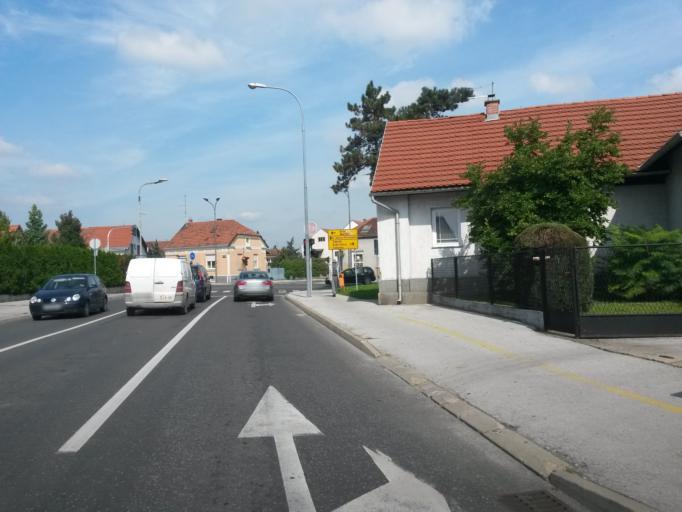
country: HR
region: Varazdinska
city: Varazdin
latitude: 46.3142
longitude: 16.3271
